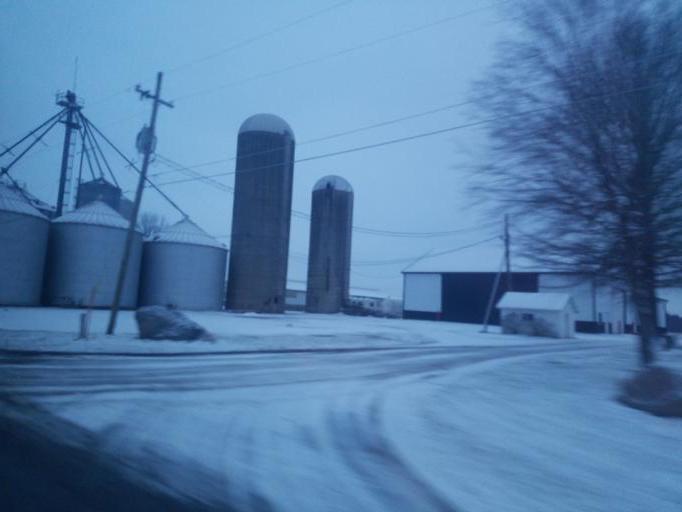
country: US
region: Ohio
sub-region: Delaware County
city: Sunbury
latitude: 40.2048
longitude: -82.8382
